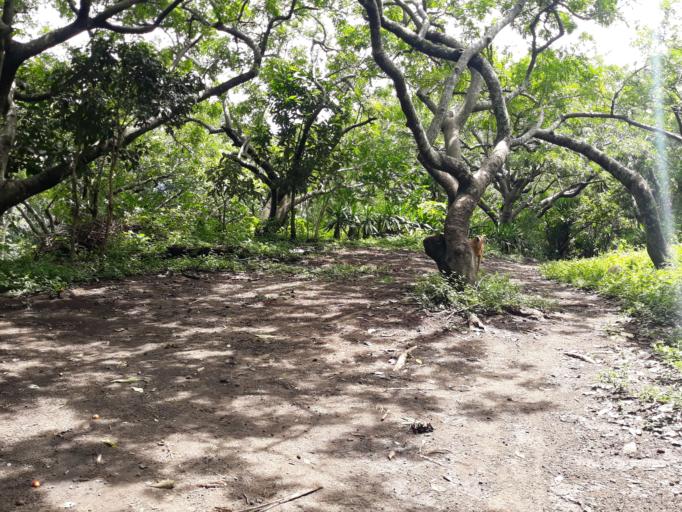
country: GT
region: Escuintla
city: San Vicente Pacaya
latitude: 14.3666
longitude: -90.5628
